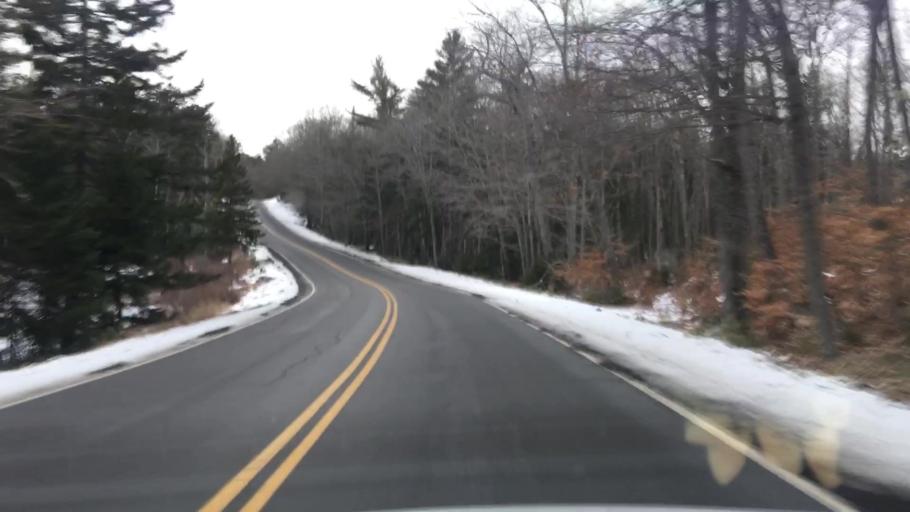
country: US
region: Maine
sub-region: Hancock County
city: Franklin
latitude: 44.6293
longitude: -68.1201
